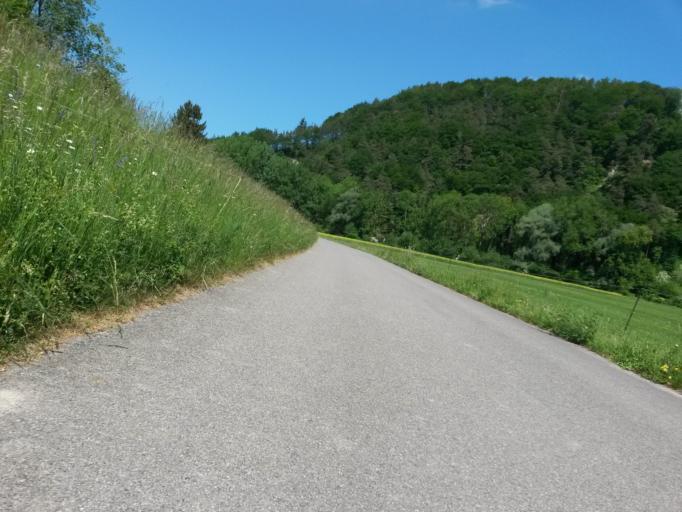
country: CH
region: Bern
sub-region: Bern-Mittelland District
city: Muhleberg
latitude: 46.9669
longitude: 7.2507
